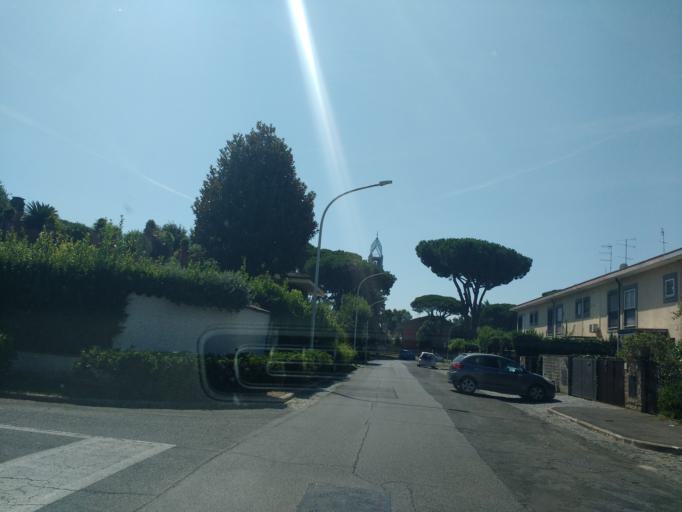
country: IT
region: Latium
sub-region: Citta metropolitana di Roma Capitale
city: Acilia-Castel Fusano-Ostia Antica
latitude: 41.7536
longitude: 12.3544
